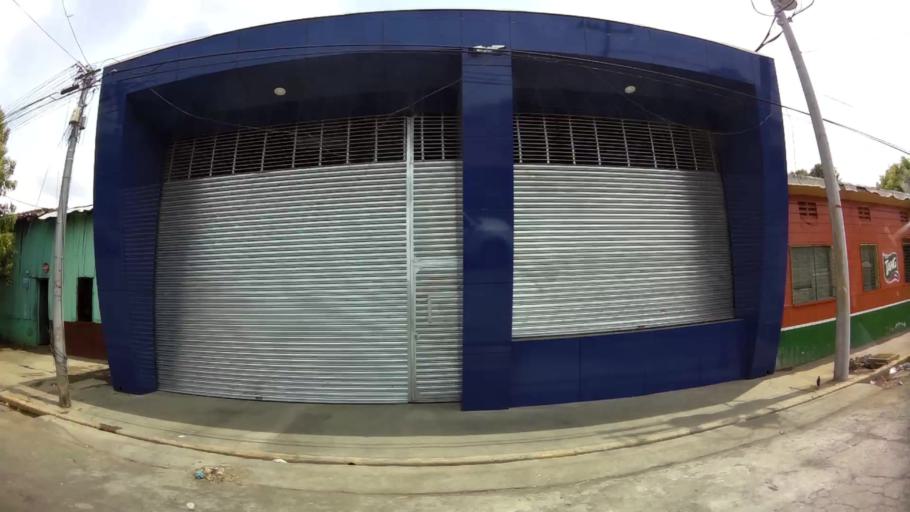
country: NI
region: Managua
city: Managua
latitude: 12.1567
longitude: -86.2884
